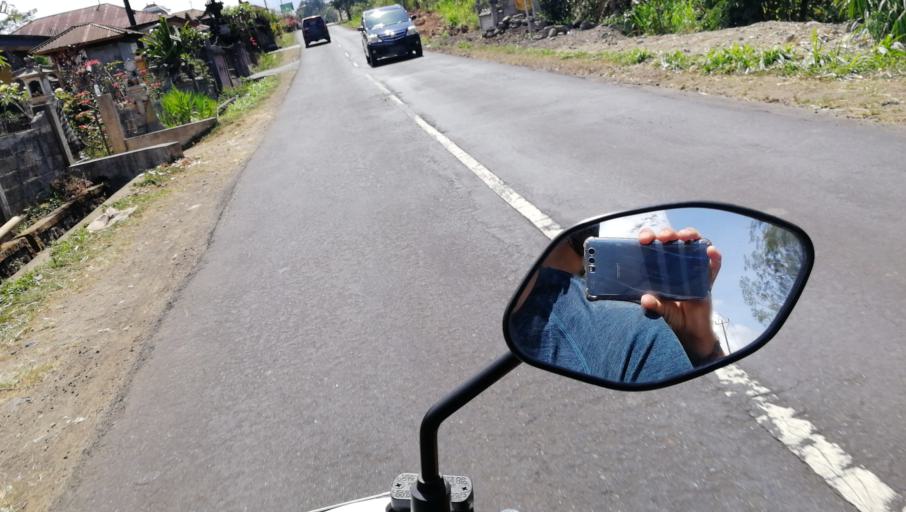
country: ID
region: Bali
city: Munduk
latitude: -8.2377
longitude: 115.1164
